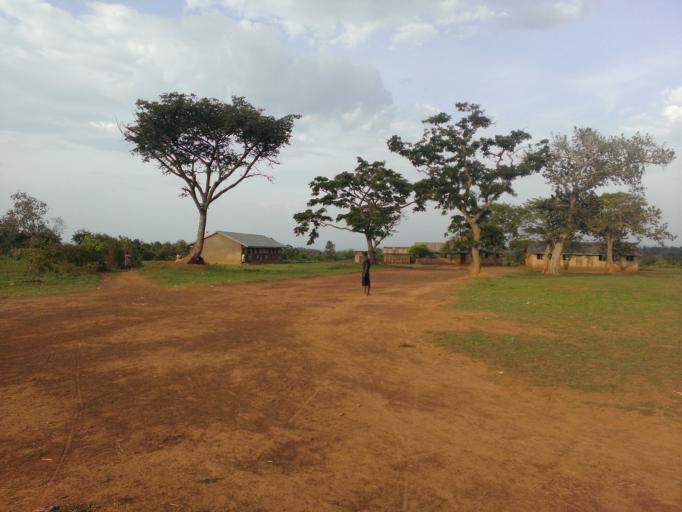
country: UG
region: Eastern Region
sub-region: Busia District
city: Busia
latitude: 0.5372
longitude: 34.0336
